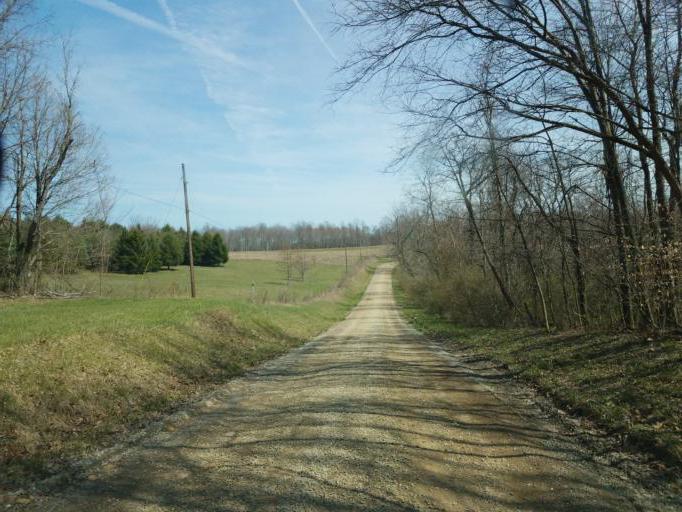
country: US
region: Ohio
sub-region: Knox County
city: Oak Hill
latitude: 40.3928
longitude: -82.1930
